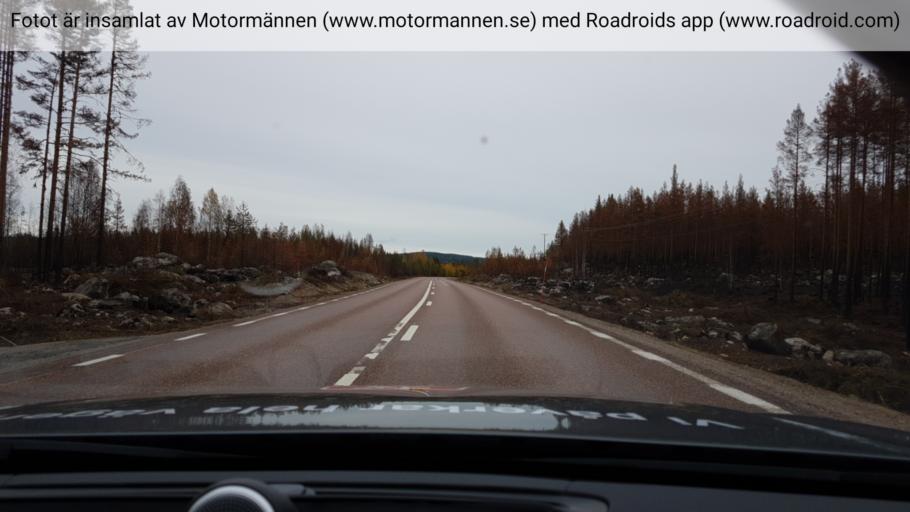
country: SE
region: Gaevleborg
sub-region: Ljusdals Kommun
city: Farila
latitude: 61.9462
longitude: 15.3964
